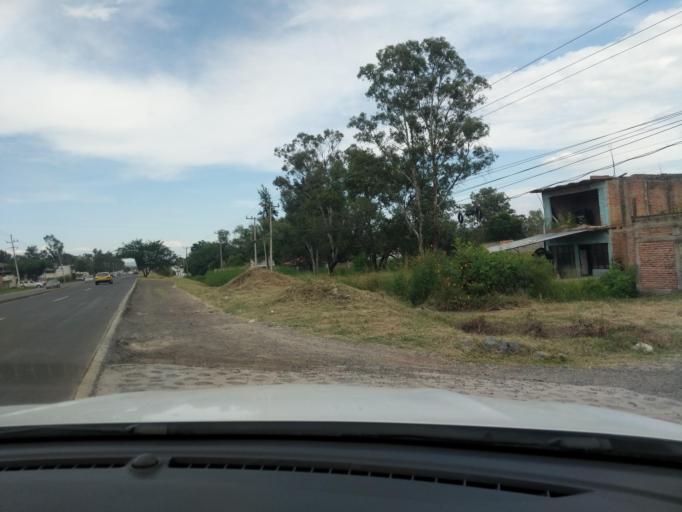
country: MX
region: Jalisco
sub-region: El Salto
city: Galaxia Bonito Jalisco
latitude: 20.5095
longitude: -103.1995
